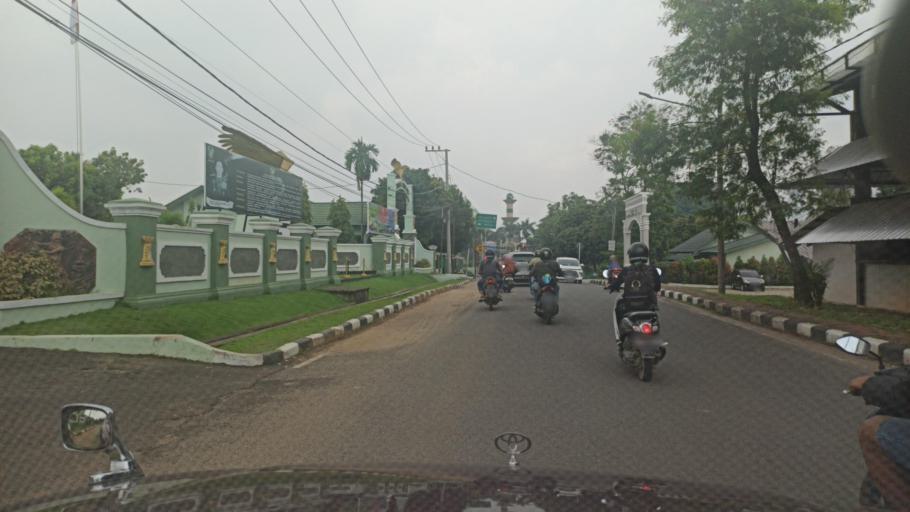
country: ID
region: South Sumatra
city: Plaju
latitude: -2.9911
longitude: 104.7437
